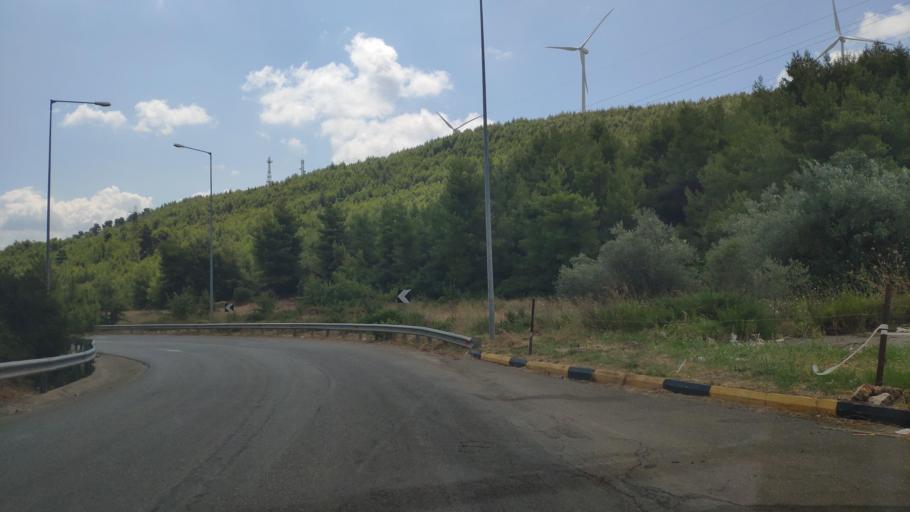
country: GR
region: Central Greece
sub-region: Nomos Fthiotidos
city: Martinon
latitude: 38.5953
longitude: 23.1890
